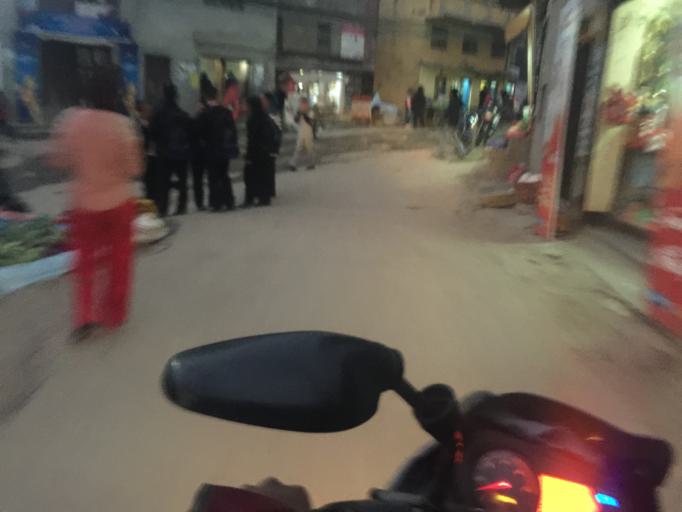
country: NP
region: Central Region
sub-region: Bagmati Zone
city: Patan
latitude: 27.6750
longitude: 85.3065
